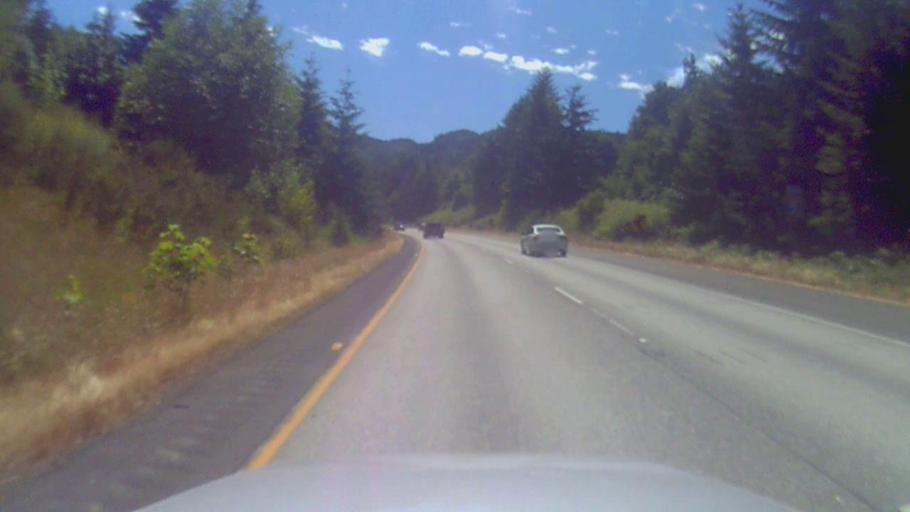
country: US
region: Washington
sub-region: Whatcom County
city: Bellingham
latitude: 48.7059
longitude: -122.4772
